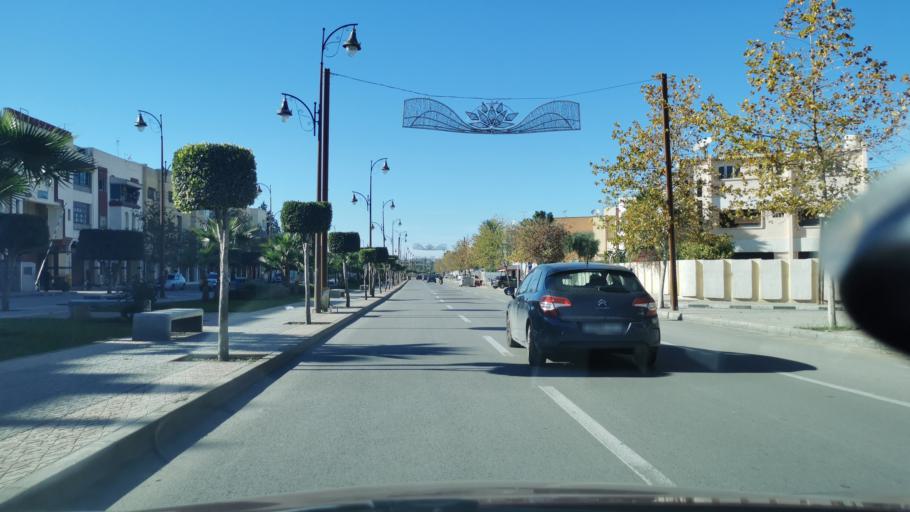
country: MA
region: Fes-Boulemane
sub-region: Fes
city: Fes
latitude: 34.0153
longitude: -5.0131
